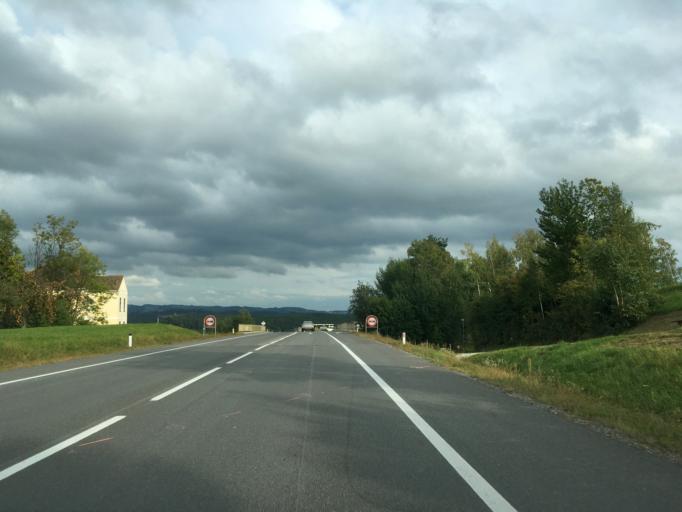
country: AT
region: Styria
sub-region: Politischer Bezirk Hartberg-Fuerstenfeld
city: Dechantskirchen
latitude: 47.4146
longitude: 16.0186
